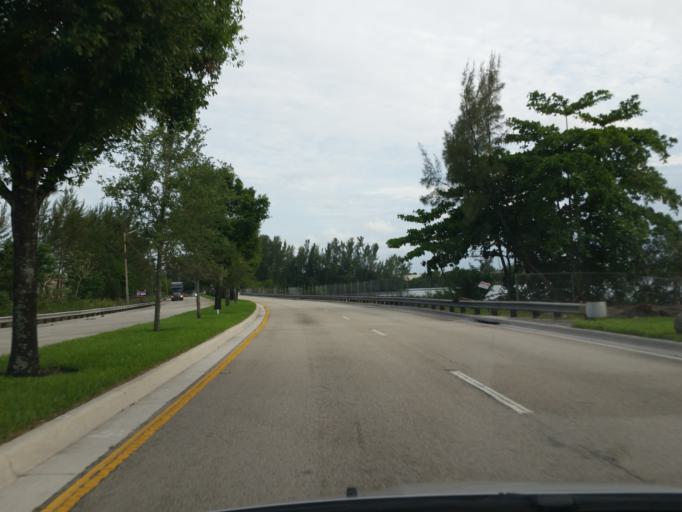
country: US
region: Florida
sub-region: Broward County
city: Broadview Park
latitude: 26.0833
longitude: -80.1810
